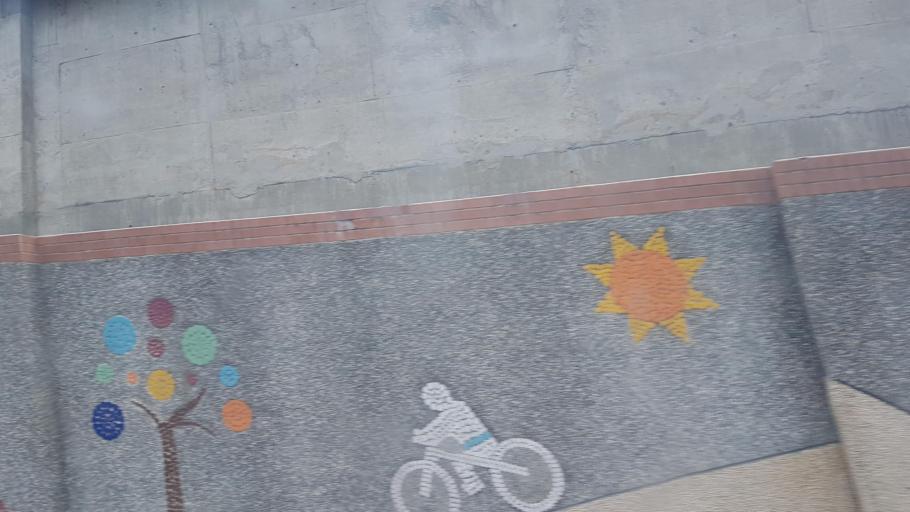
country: TW
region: Taiwan
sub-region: Hualien
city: Hualian
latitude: 24.0034
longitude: 121.6394
